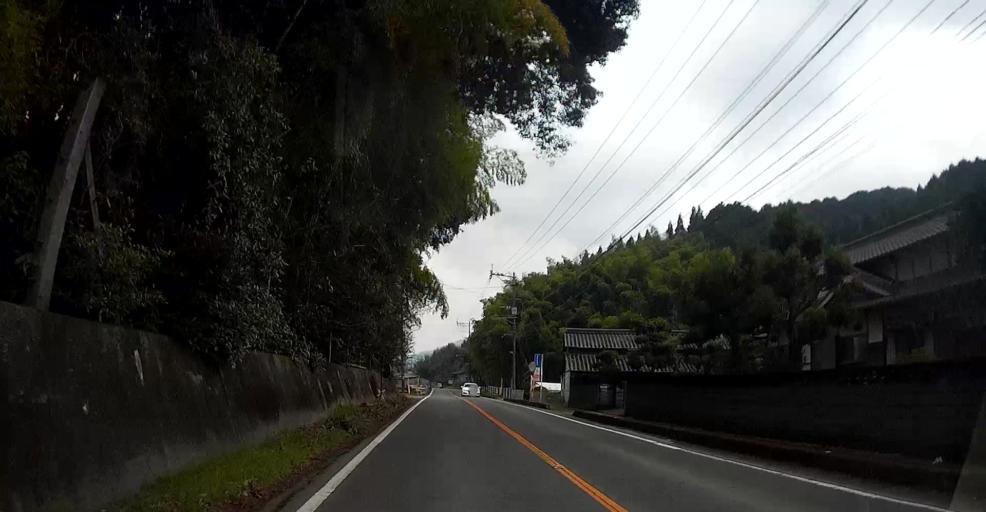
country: JP
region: Kumamoto
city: Matsubase
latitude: 32.6447
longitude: 130.7329
